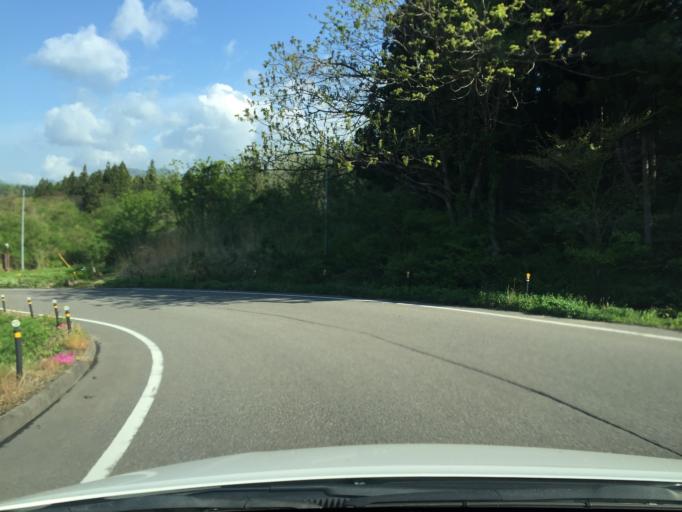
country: JP
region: Fukushima
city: Kitakata
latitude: 37.6858
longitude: 139.6752
